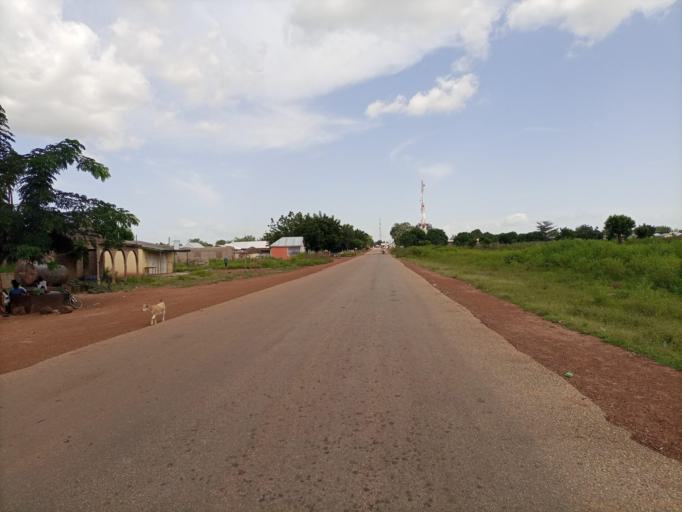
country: GH
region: Northern
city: Savelugu
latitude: 9.5627
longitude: -0.9572
